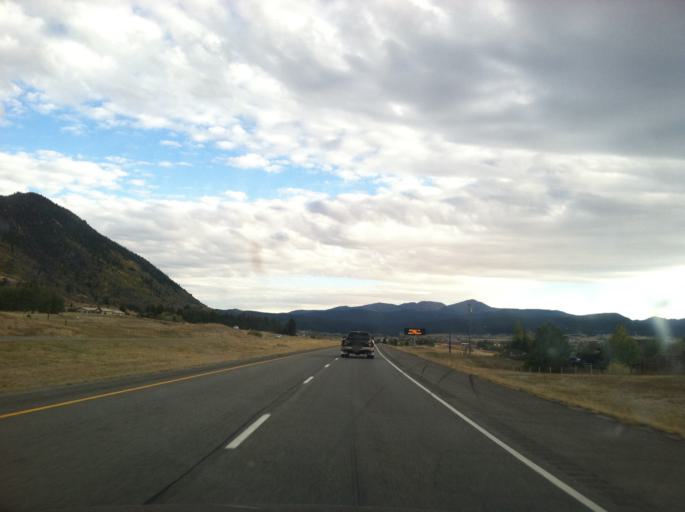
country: US
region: Montana
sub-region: Silver Bow County
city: Butte
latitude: 45.9756
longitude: -112.4771
